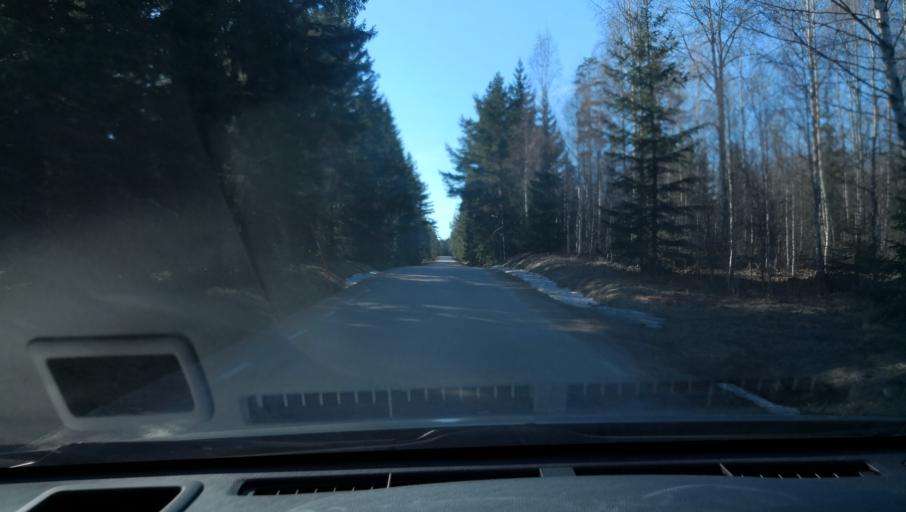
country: SE
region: Dalarna
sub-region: Avesta Kommun
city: Horndal
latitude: 60.0846
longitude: 16.4264
